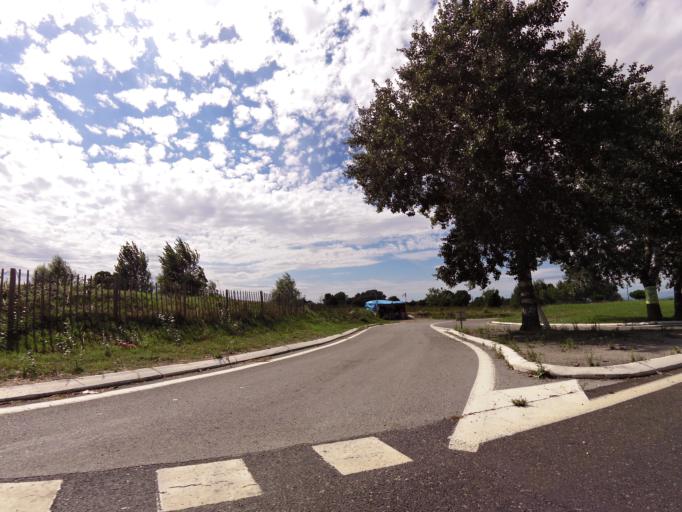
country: FR
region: Languedoc-Roussillon
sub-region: Departement du Gard
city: Le Grau-du-Roi
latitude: 43.5598
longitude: 4.1522
